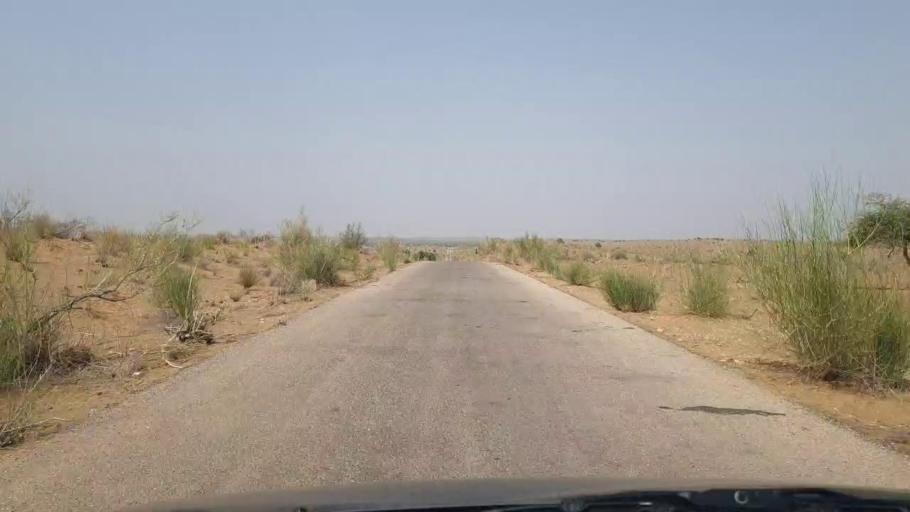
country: PK
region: Sindh
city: Chor
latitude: 25.4674
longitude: 70.4942
